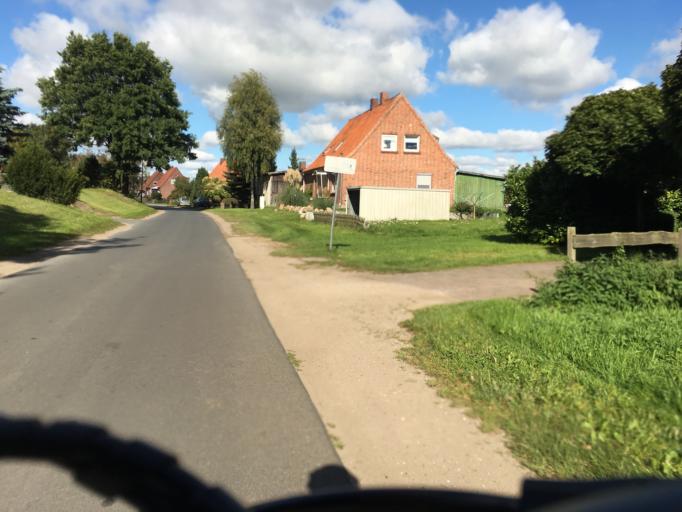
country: DE
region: Lower Saxony
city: Bardowick
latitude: 53.3091
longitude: 10.3807
